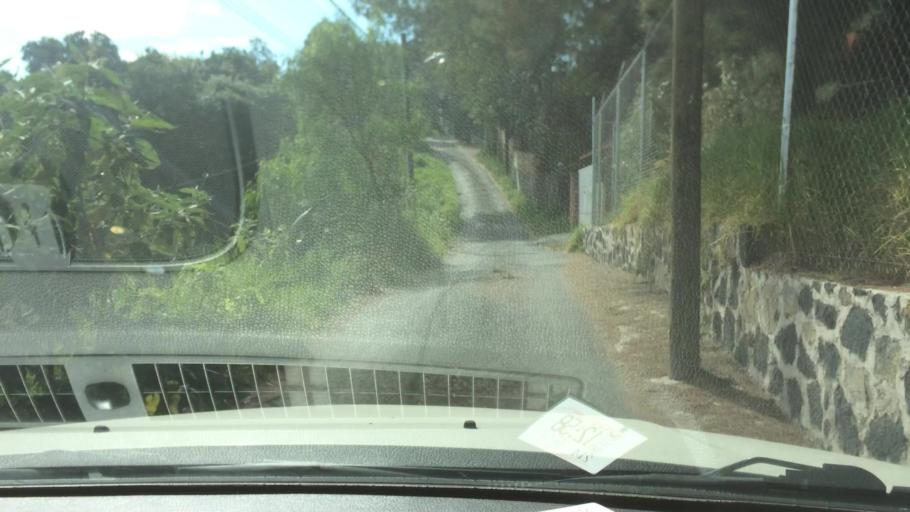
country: MX
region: Mexico City
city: Xochimilco
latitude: 19.2352
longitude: -99.1544
